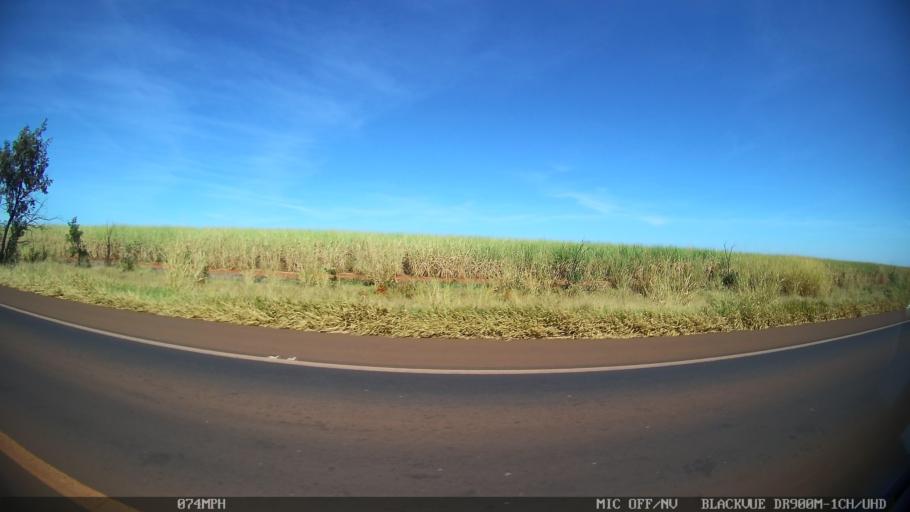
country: BR
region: Sao Paulo
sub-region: Sao Joaquim Da Barra
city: Sao Joaquim da Barra
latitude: -20.5577
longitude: -47.7059
